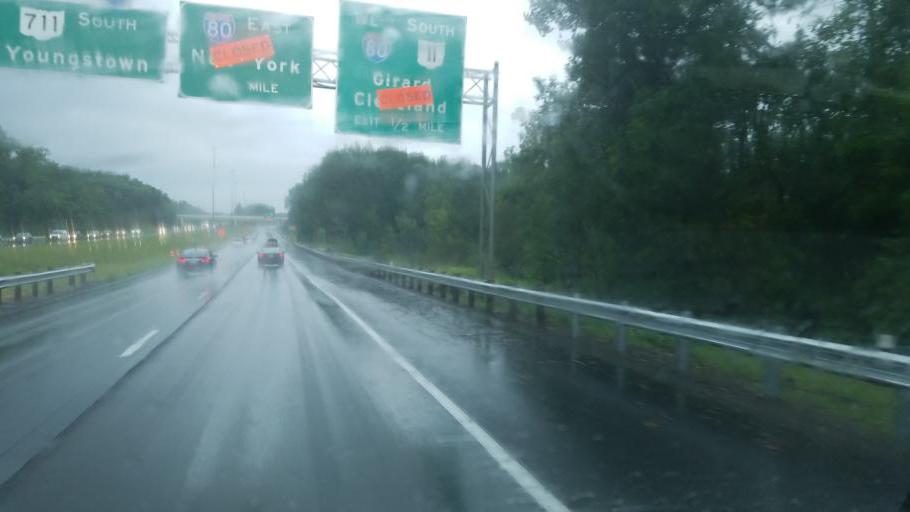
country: US
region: Ohio
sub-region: Trumbull County
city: Churchill
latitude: 41.1578
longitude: -80.6776
